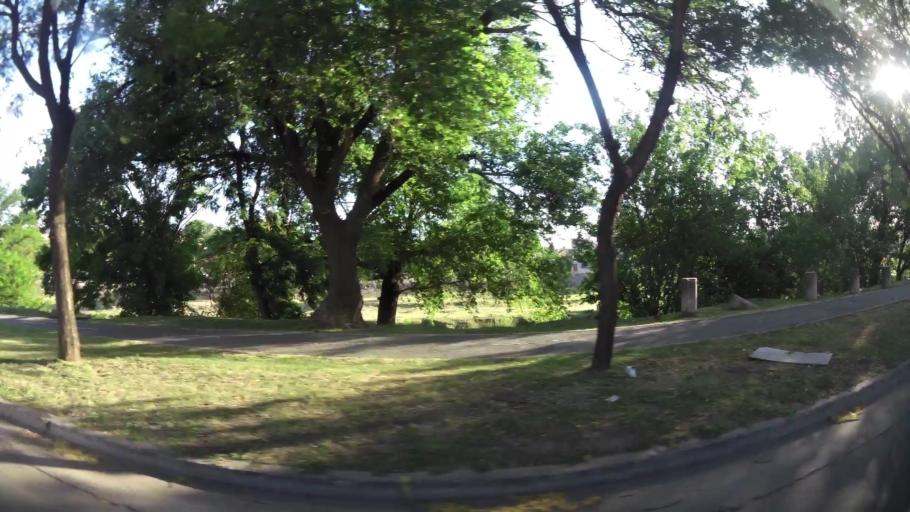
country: AR
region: Cordoba
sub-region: Departamento de Capital
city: Cordoba
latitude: -31.3950
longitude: -64.2205
